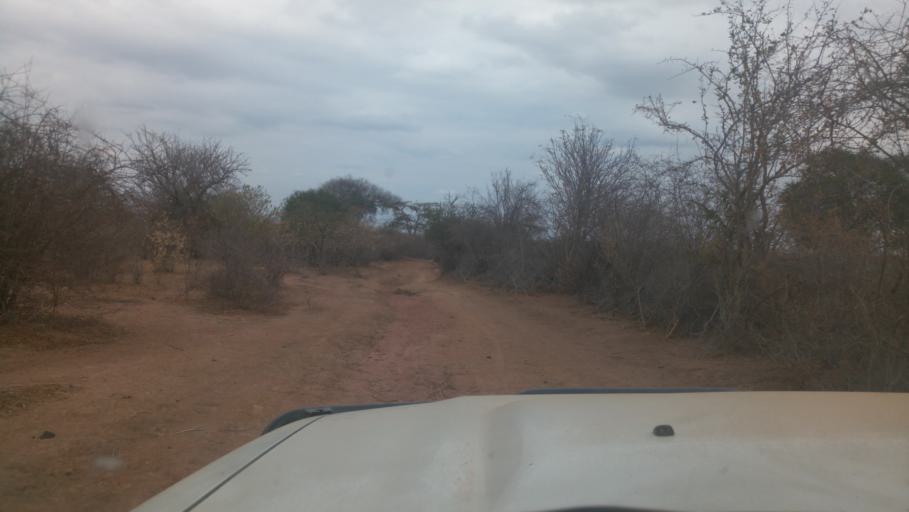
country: KE
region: Kitui
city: Kitui
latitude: -1.6174
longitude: 37.9220
